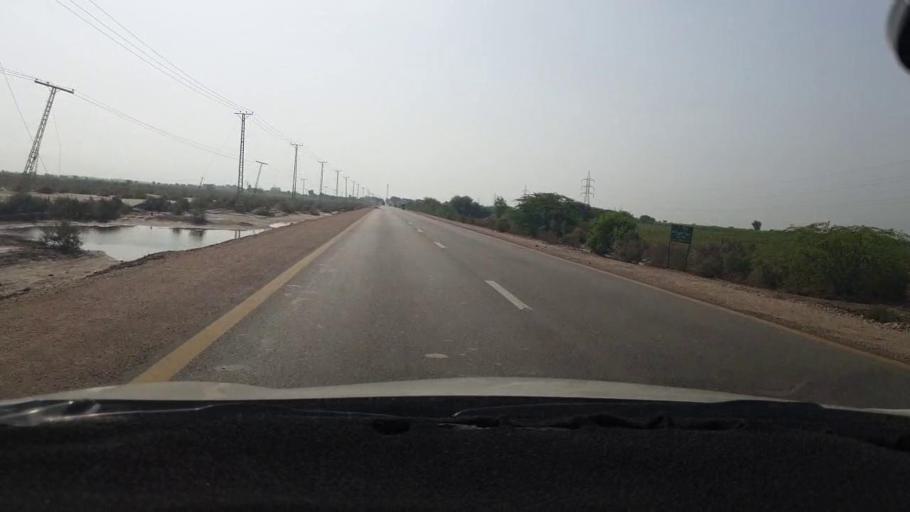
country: PK
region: Sindh
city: Jhol
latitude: 25.9496
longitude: 68.9798
